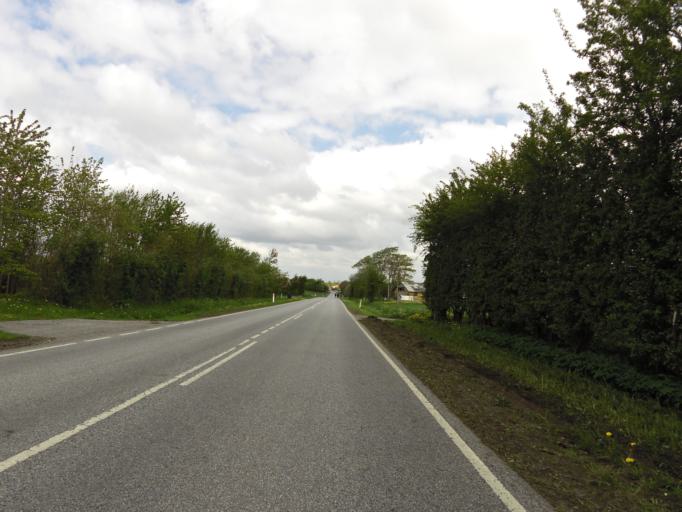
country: DK
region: South Denmark
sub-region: Haderslev Kommune
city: Gram
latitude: 55.2386
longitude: 8.9654
